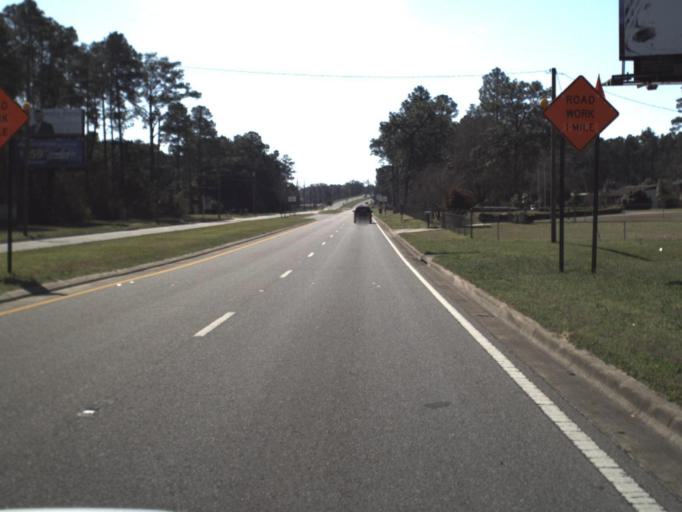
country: US
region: Florida
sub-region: Jackson County
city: Marianna
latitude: 30.7447
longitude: -85.1869
